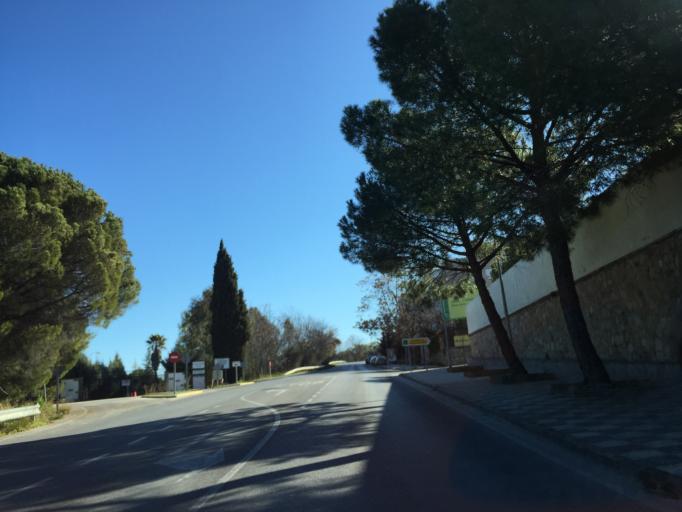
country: ES
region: Andalusia
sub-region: Provincia de Malaga
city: Ronda
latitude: 36.7551
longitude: -5.1696
